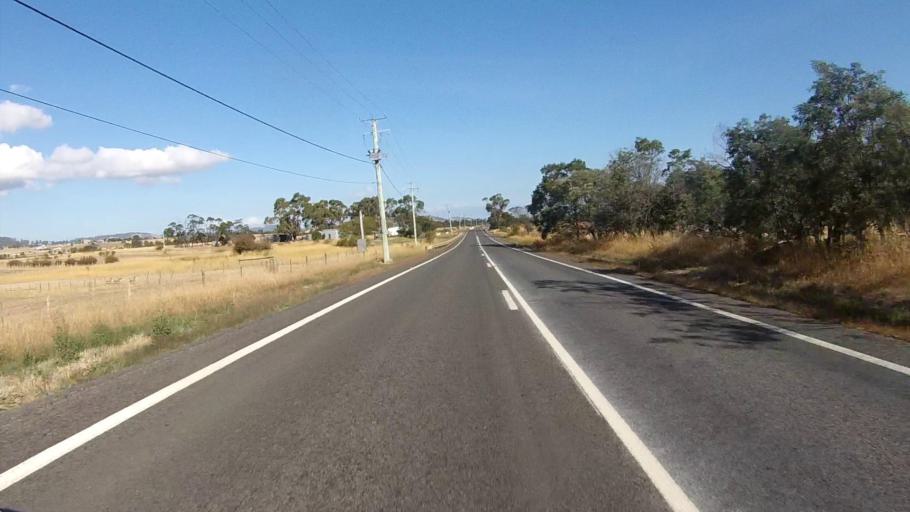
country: AU
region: Tasmania
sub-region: Sorell
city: Sorell
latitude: -42.7175
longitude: 147.5176
